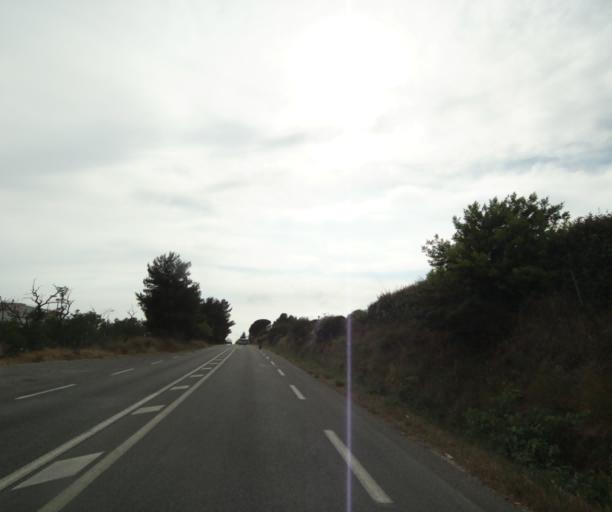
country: FR
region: Provence-Alpes-Cote d'Azur
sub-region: Departement du Var
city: La Garde
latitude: 43.1433
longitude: 6.0101
